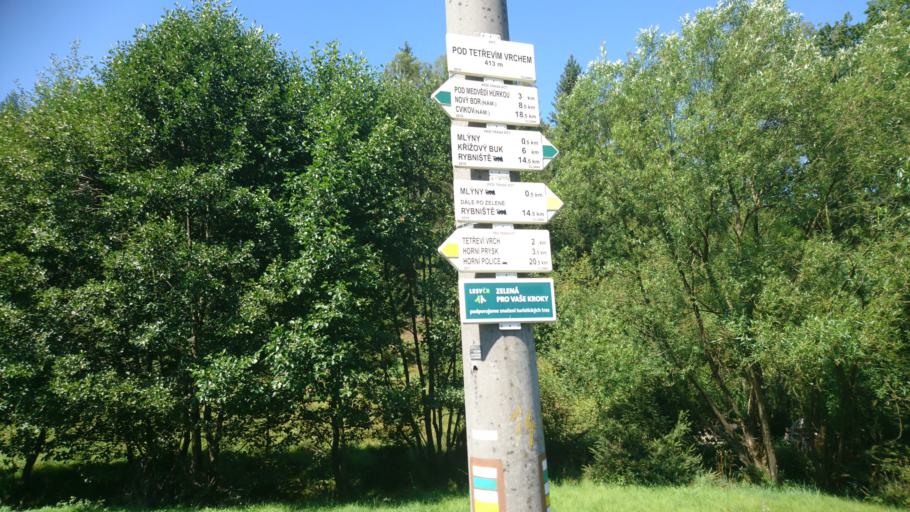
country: CZ
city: Kamenicky Senov
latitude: 50.8100
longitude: 14.4978
